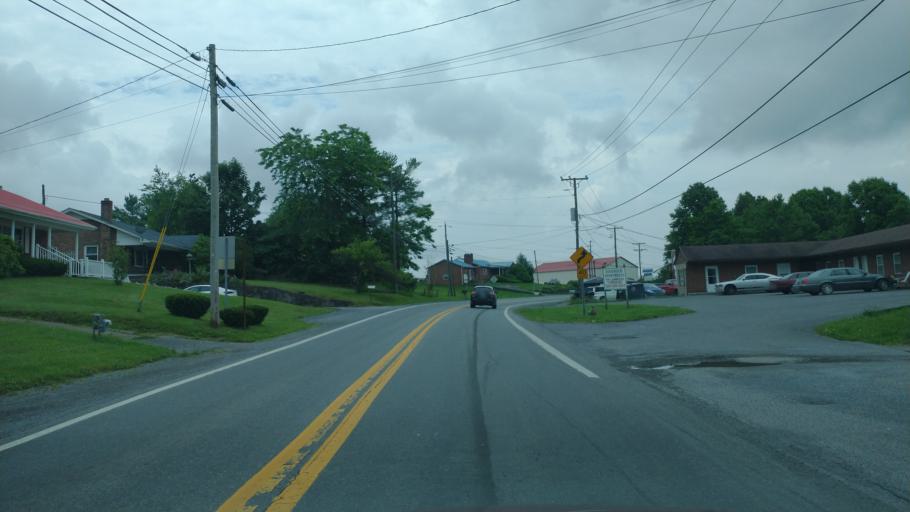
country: US
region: West Virginia
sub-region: Mercer County
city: Athens
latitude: 37.4159
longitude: -81.0159
